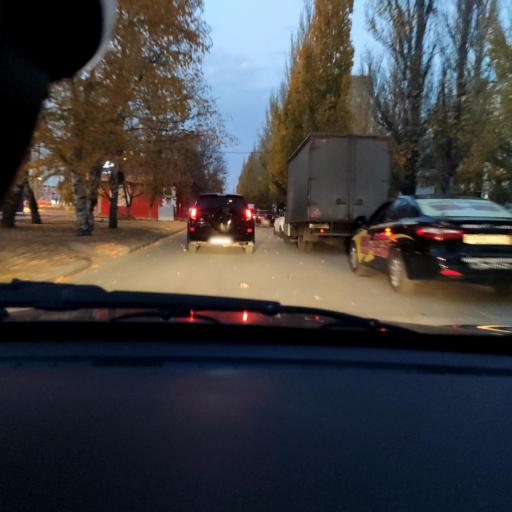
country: RU
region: Samara
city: Tol'yatti
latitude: 53.5338
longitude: 49.2992
